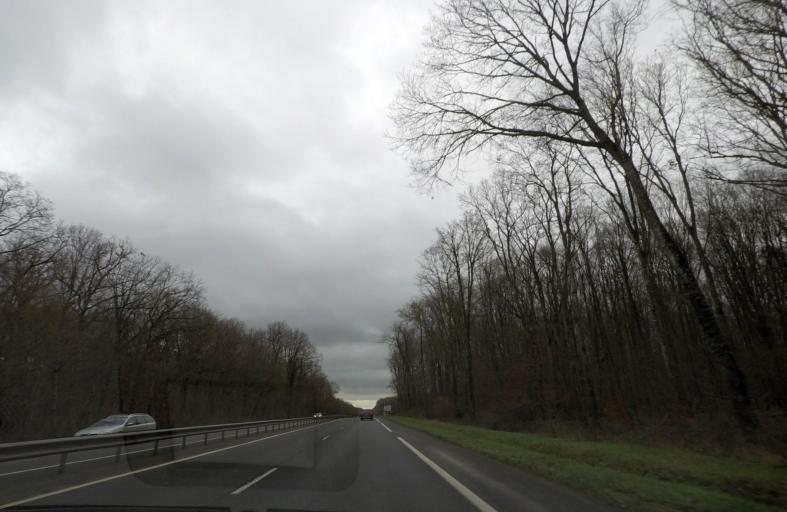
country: FR
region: Centre
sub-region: Departement du Loir-et-Cher
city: Cellettes
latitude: 47.5469
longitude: 1.3956
